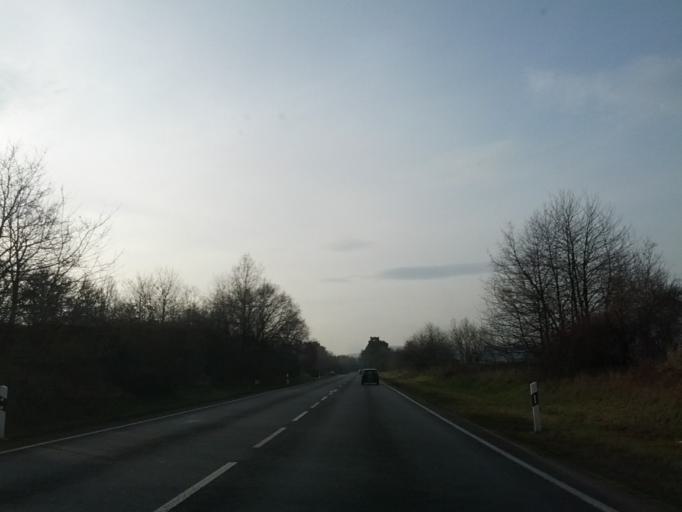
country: DE
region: Thuringia
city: Barchfeld
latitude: 50.7928
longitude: 10.3188
